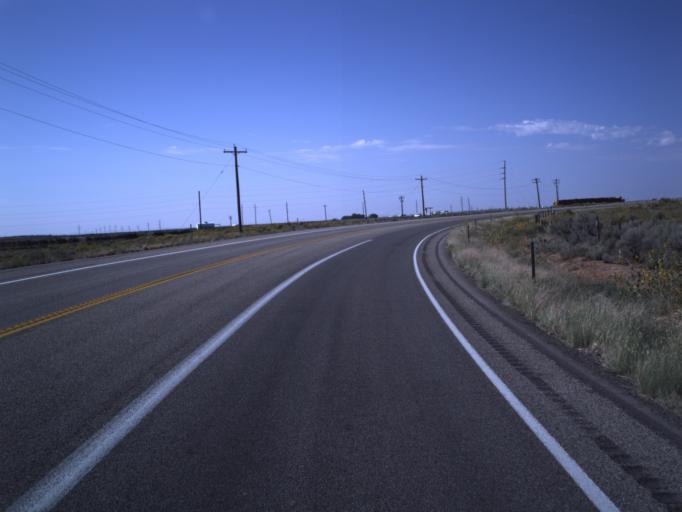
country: US
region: Utah
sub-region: San Juan County
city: Blanding
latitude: 37.5763
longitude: -109.4785
